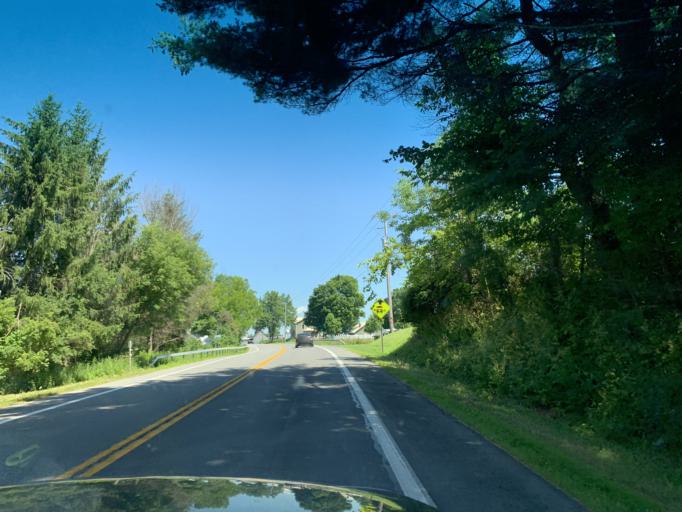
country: US
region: New York
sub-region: Oneida County
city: Waterville
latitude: 42.8905
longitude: -75.2470
